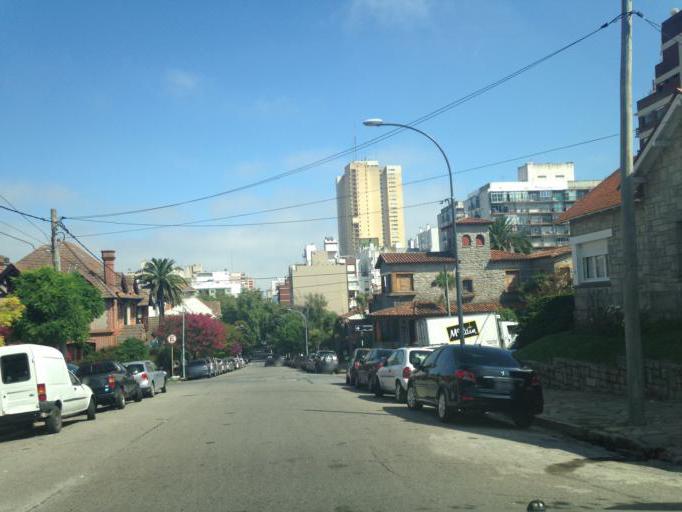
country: AR
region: Buenos Aires
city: Mar del Plata
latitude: -38.0116
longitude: -57.5365
